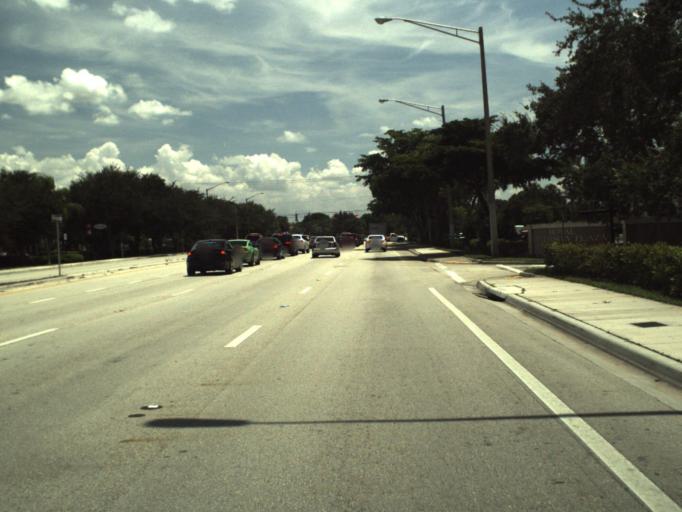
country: US
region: Florida
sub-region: Broward County
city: Coral Springs
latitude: 26.2611
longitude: -80.2501
